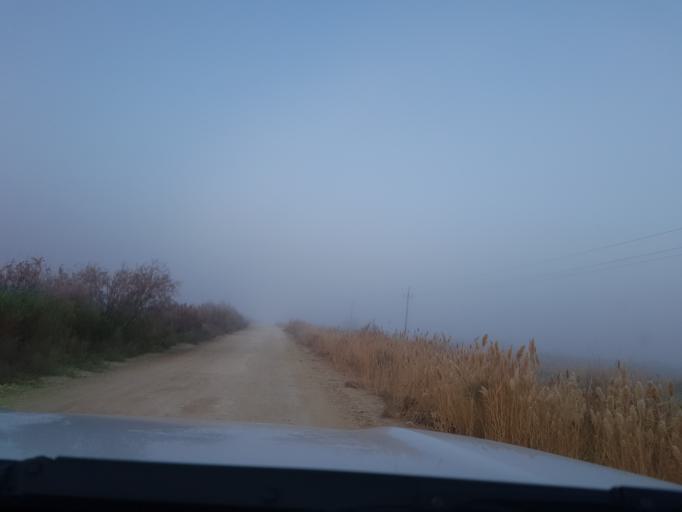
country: TM
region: Dasoguz
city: Koeneuergench
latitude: 41.8452
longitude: 58.4556
